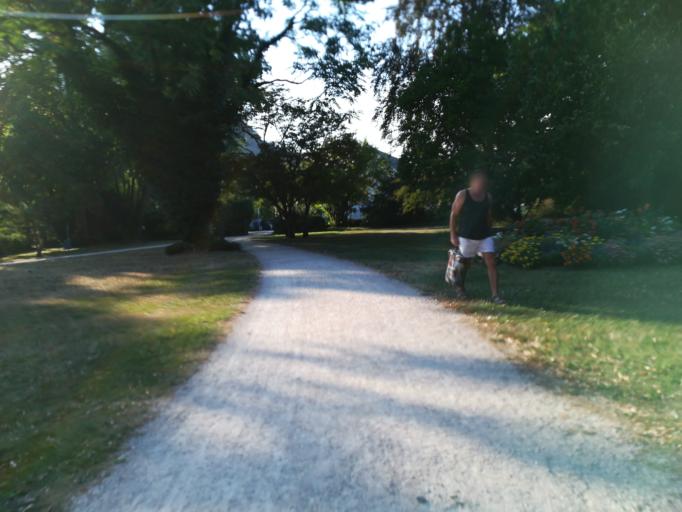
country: DE
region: Baden-Wuerttemberg
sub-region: Freiburg Region
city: Singen
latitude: 47.7614
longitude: 8.8299
